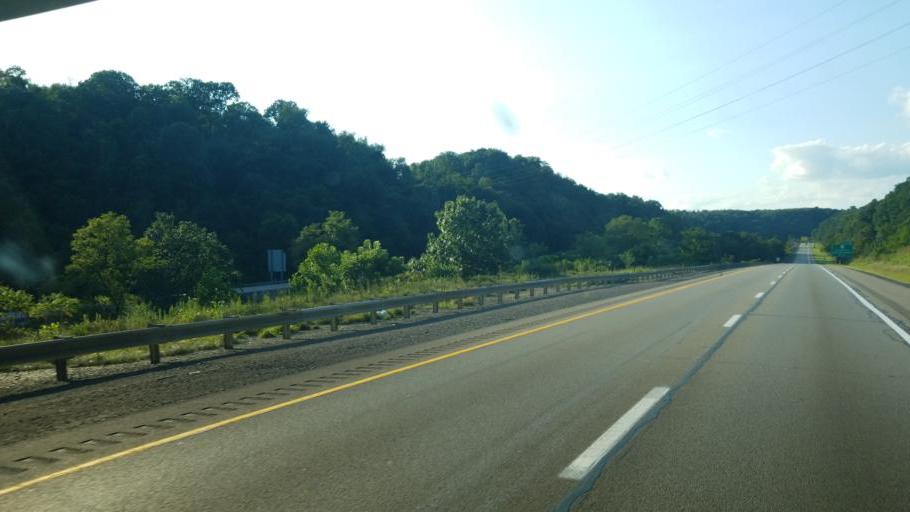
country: US
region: Pennsylvania
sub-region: Allegheny County
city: Emsworth
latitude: 40.4805
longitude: -80.1204
